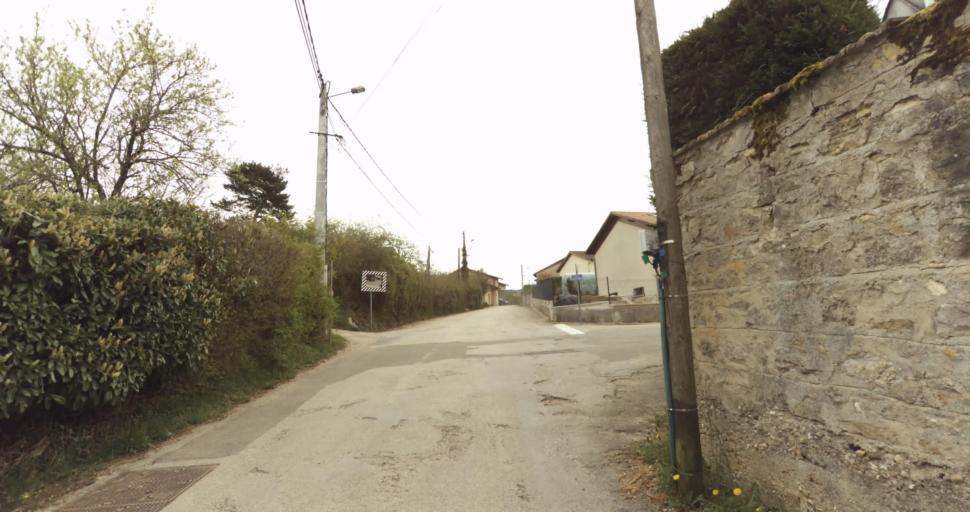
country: FR
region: Rhone-Alpes
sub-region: Departement de l'Ain
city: Amberieu-en-Bugey
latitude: 45.9653
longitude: 5.3645
